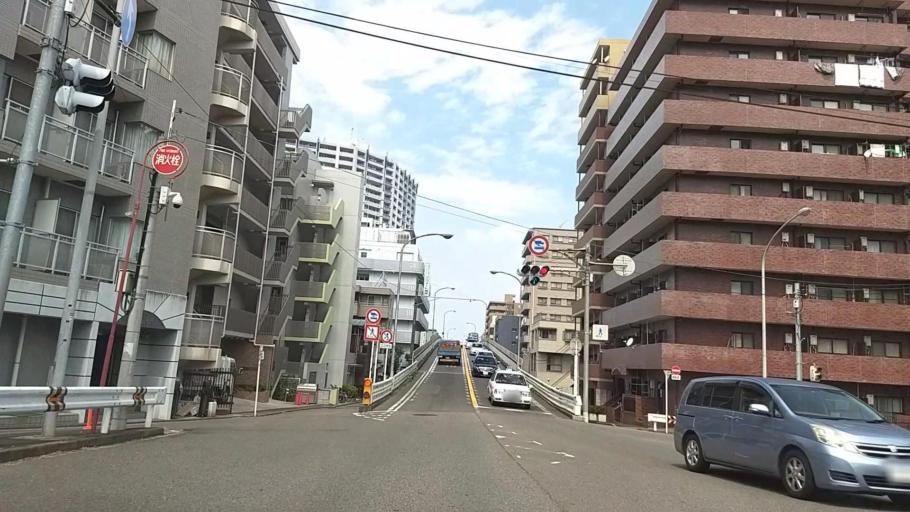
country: JP
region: Kanagawa
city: Yokohama
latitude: 35.4576
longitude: 139.6174
